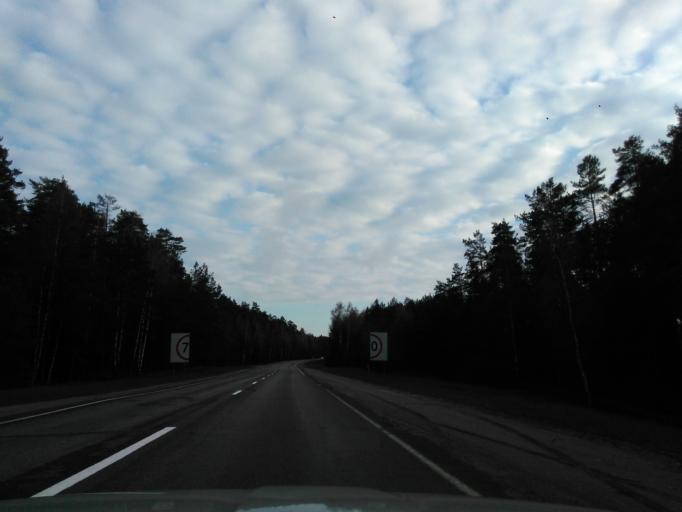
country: BY
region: Minsk
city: Plyeshchanitsy
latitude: 54.3468
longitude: 27.8793
